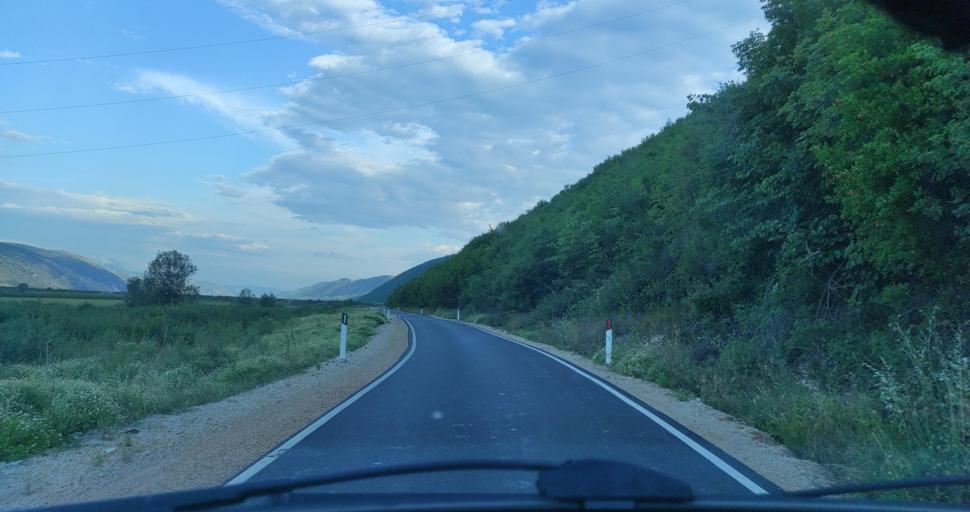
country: AL
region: Shkoder
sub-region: Rrethi i Shkodres
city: Velipoje
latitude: 41.9270
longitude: 19.4475
